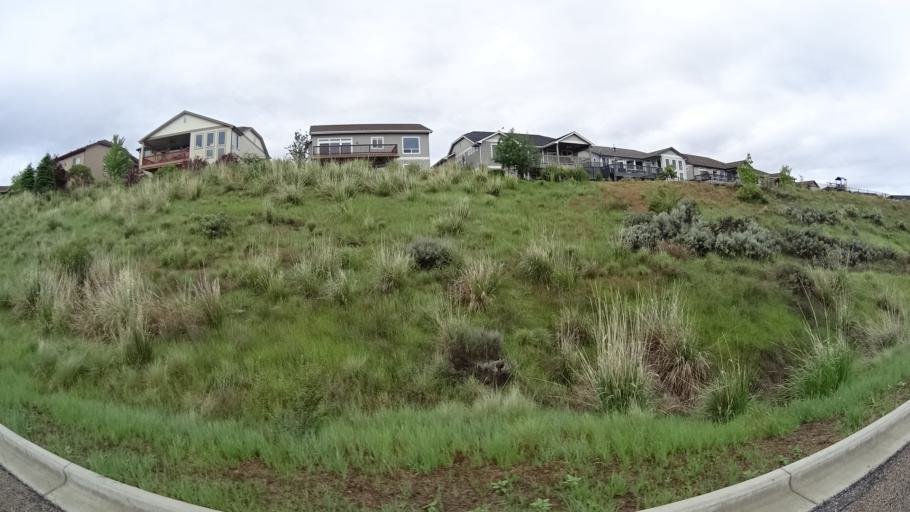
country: US
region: Idaho
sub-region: Ada County
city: Eagle
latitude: 43.7691
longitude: -116.2578
